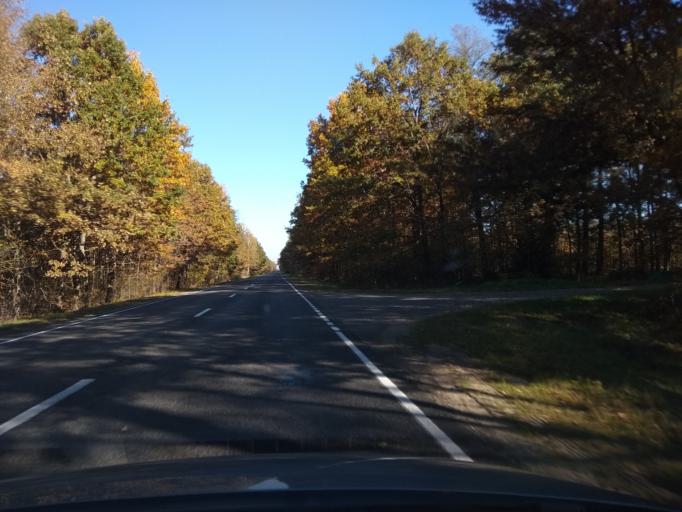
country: BY
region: Brest
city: Malaryta
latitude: 51.9130
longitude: 24.1543
